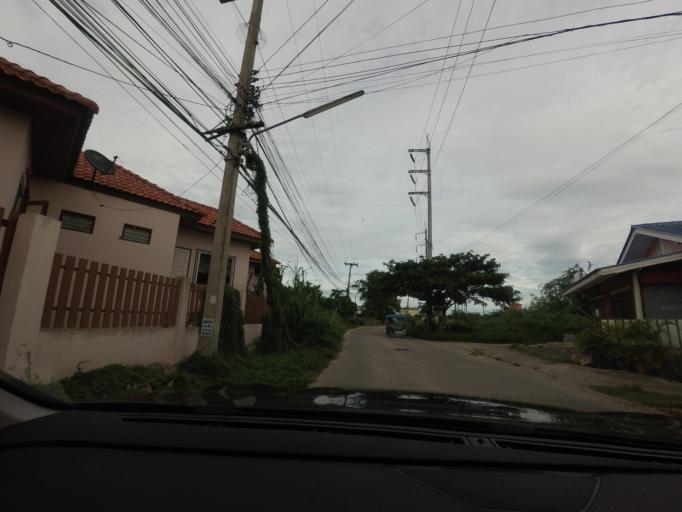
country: TH
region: Prachuap Khiri Khan
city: Hua Hin
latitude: 12.5382
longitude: 99.9542
